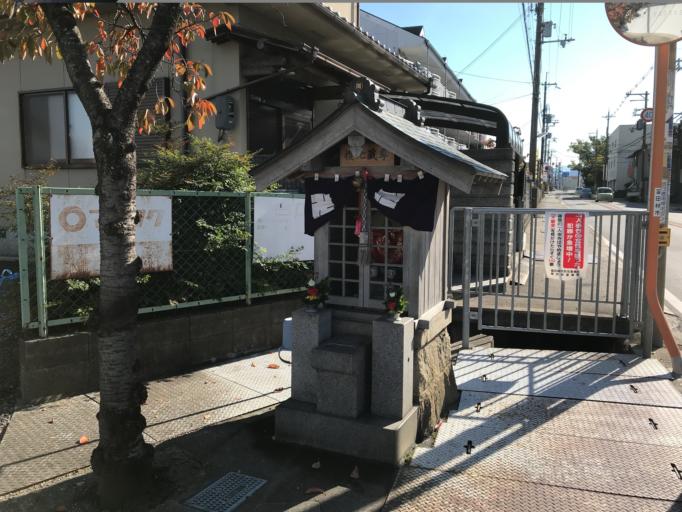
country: JP
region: Osaka
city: Tondabayashicho
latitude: 34.5197
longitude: 135.6099
